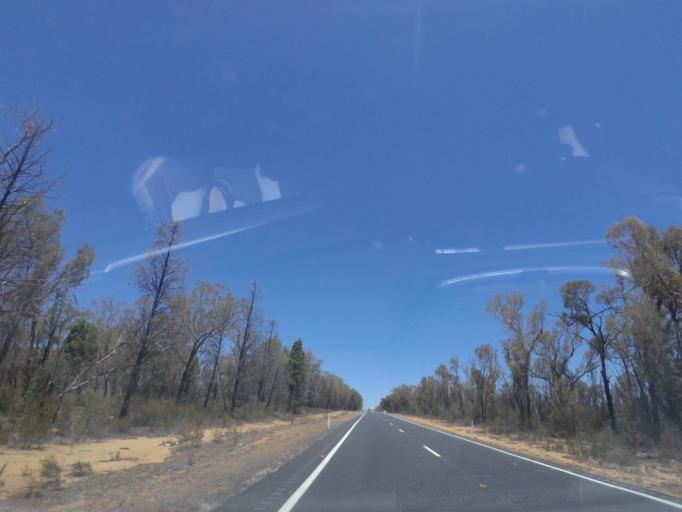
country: AU
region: New South Wales
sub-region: Warrumbungle Shire
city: Coonabarabran
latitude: -30.9590
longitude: 149.4200
